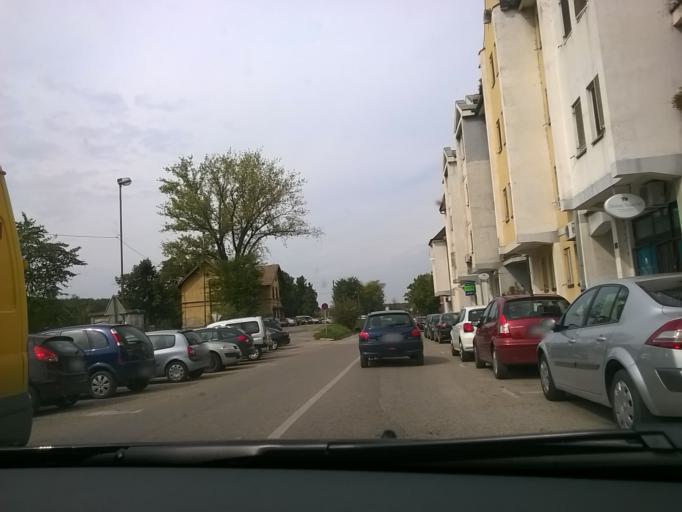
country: RS
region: Autonomna Pokrajina Vojvodina
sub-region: Juznobanatski Okrug
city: Pancevo
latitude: 44.8689
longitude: 20.6383
